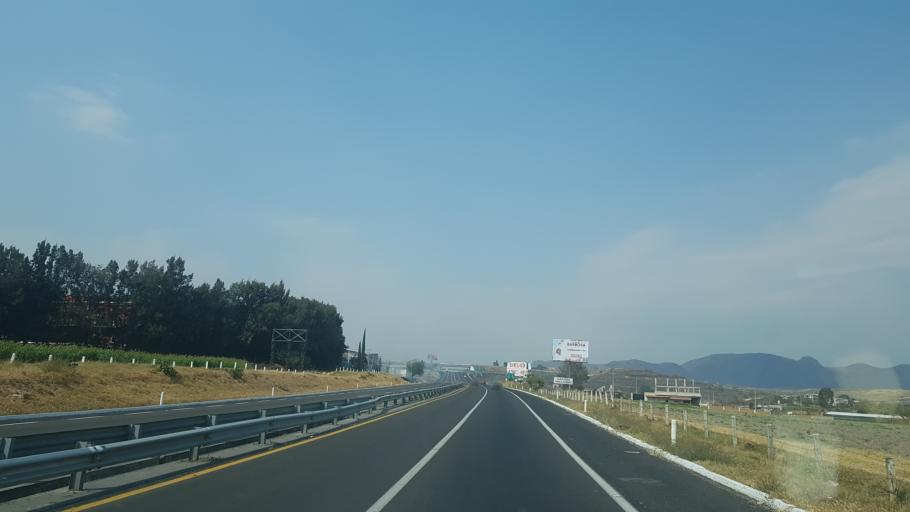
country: MX
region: Puebla
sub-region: Atlixco
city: San Agustin Huixaxtla
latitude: 18.9311
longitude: -98.3955
